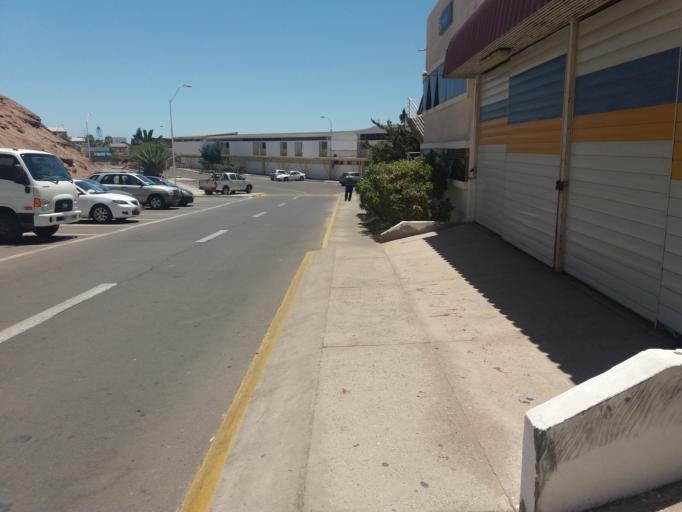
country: CL
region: Antofagasta
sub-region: Provincia de Antofagasta
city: Antofagasta
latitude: -23.6814
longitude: -70.4094
